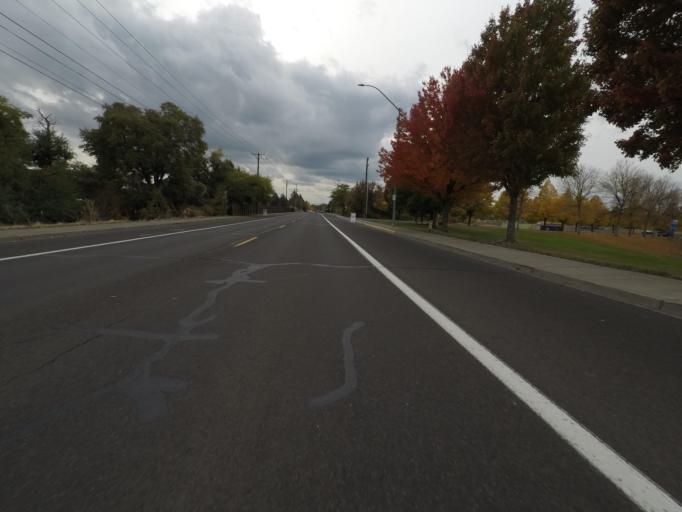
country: US
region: Washington
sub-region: Walla Walla County
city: Walla Walla East
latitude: 46.0727
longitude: -118.2872
